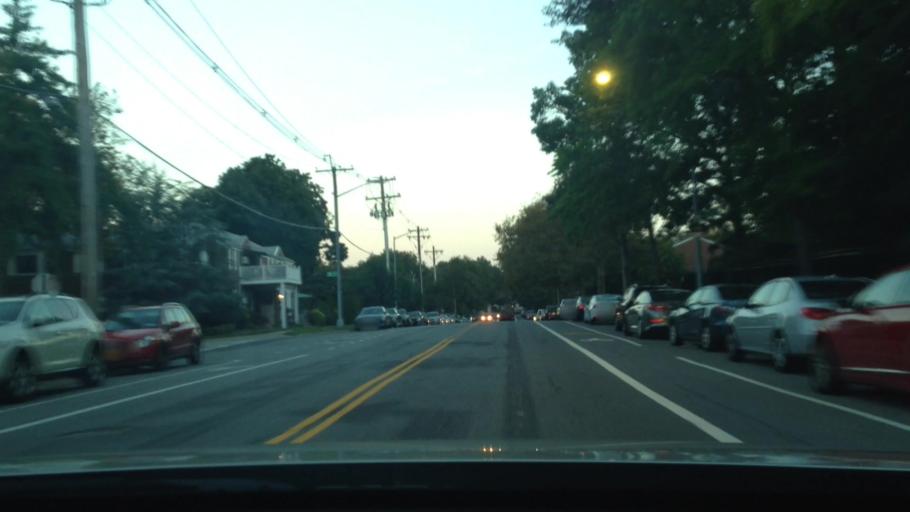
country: US
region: New York
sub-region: Nassau County
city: North New Hyde Park
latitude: 40.7501
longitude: -73.7123
